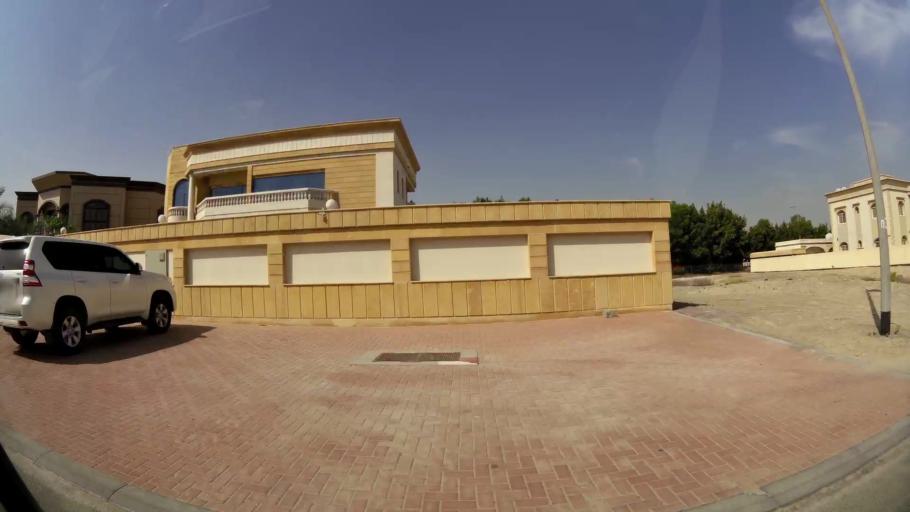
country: AE
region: Ash Shariqah
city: Sharjah
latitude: 25.2660
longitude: 55.4078
